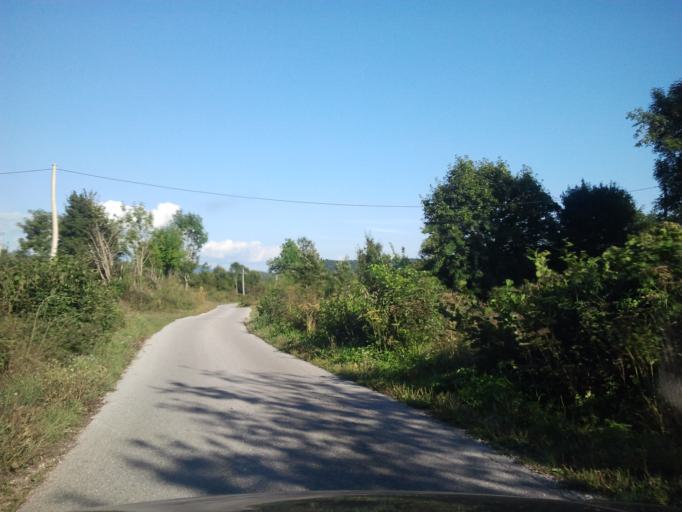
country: HR
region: Zadarska
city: Obrovac
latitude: 44.3536
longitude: 15.6684
